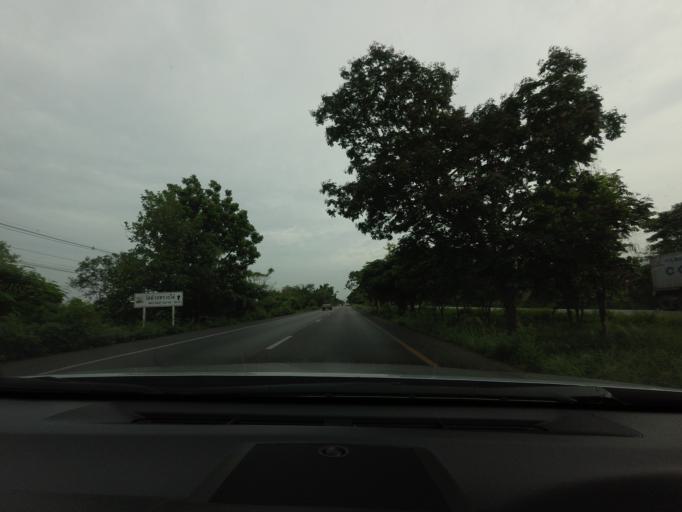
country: TH
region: Phetchaburi
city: Cha-am
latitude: 12.7653
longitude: 99.9346
